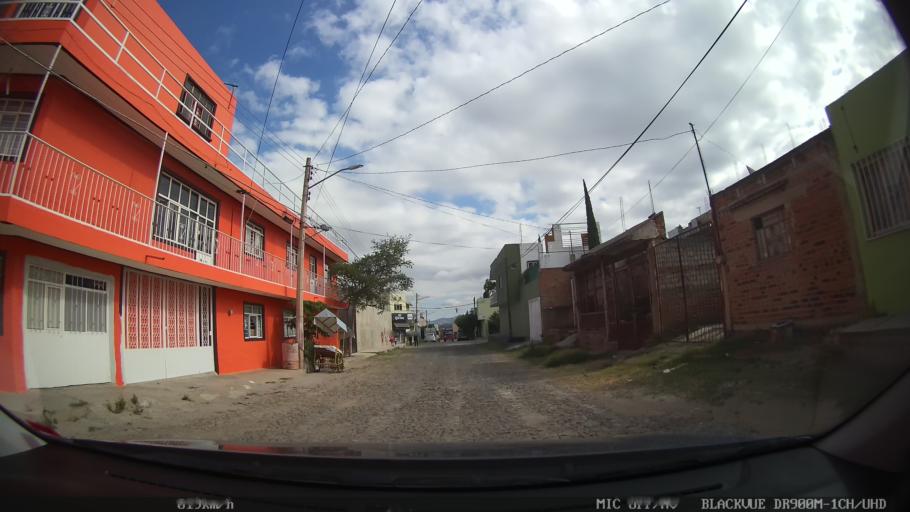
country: MX
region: Jalisco
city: Tlaquepaque
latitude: 20.6837
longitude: -103.2574
